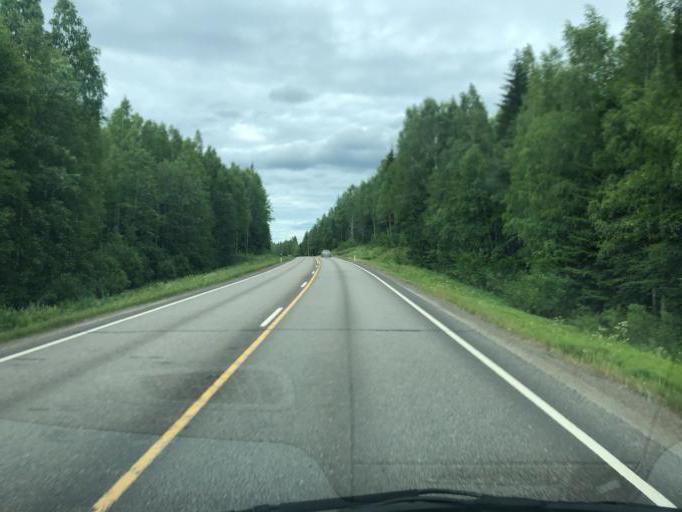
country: FI
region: Kymenlaakso
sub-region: Kouvola
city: Kouvola
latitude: 61.0060
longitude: 26.9462
